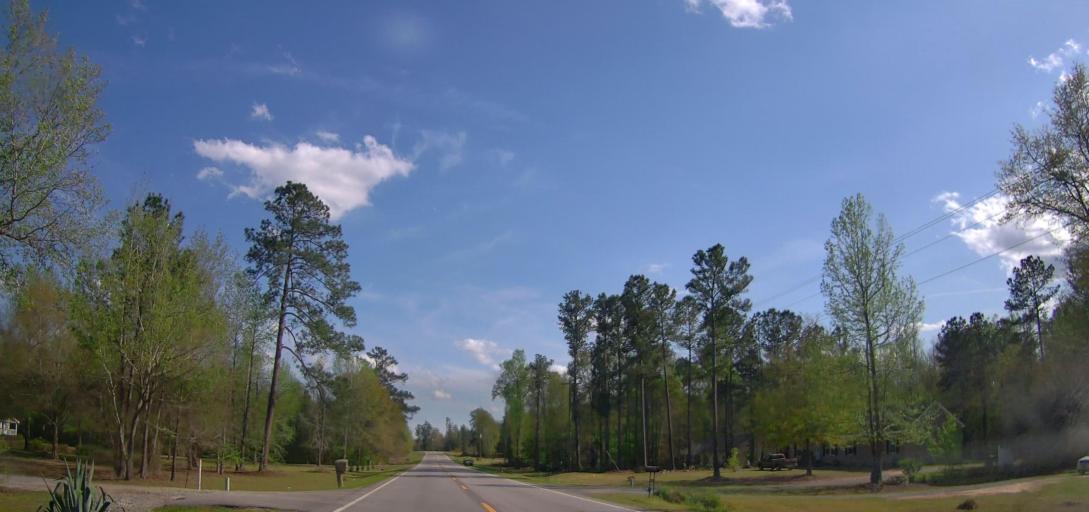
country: US
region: Georgia
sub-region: Baldwin County
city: Hardwick
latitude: 33.0695
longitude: -83.1354
